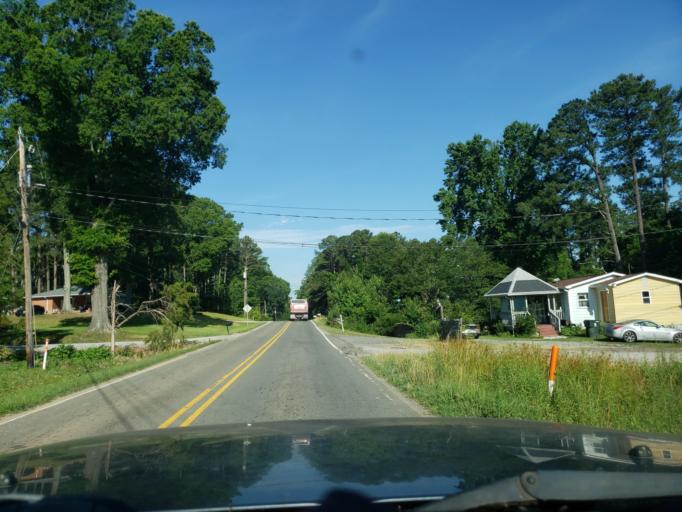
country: US
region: North Carolina
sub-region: Durham County
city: Durham
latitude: 35.9559
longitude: -78.8536
